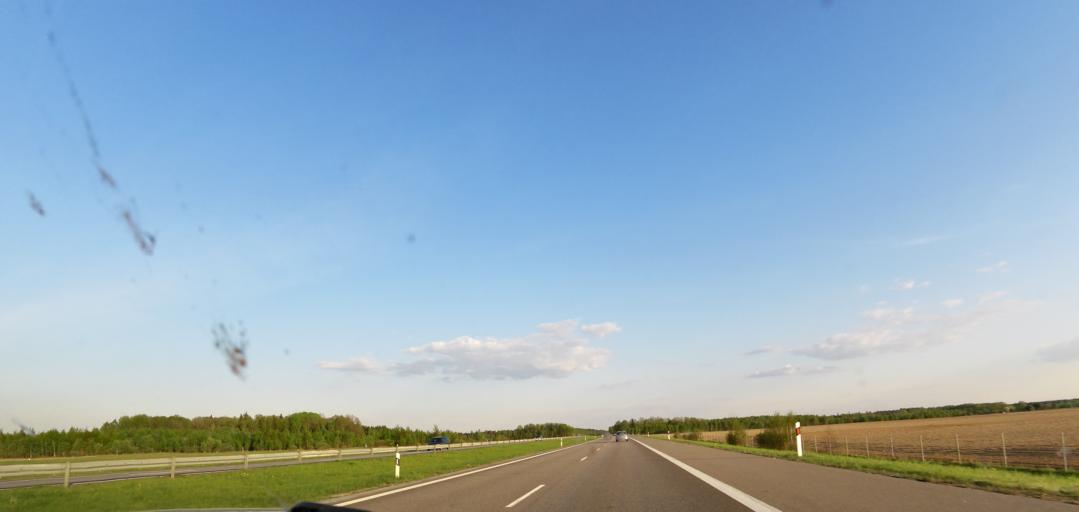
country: LT
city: Sirvintos
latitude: 54.9868
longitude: 24.9335
